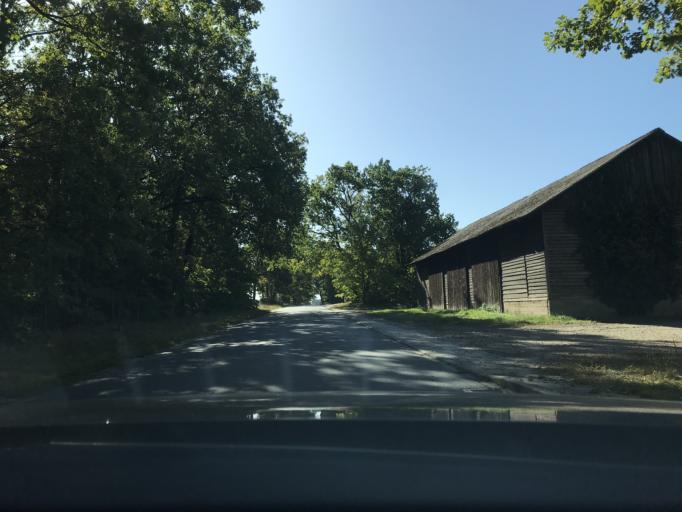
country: DE
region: Lower Saxony
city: Gerdau
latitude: 52.9506
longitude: 10.4003
